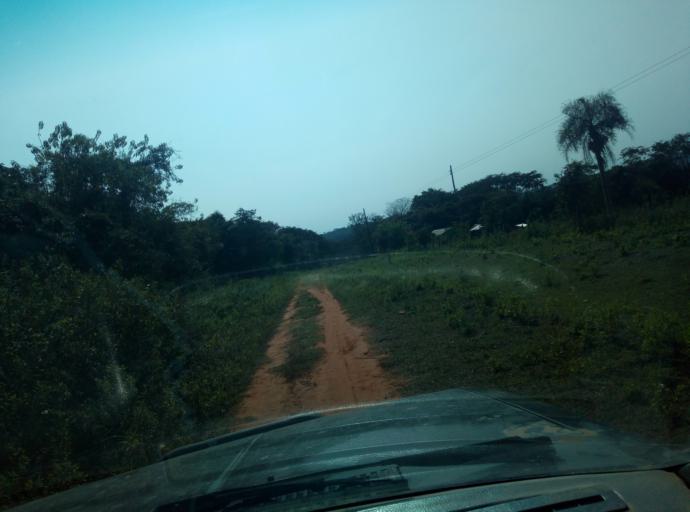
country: PY
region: Caaguazu
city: Carayao
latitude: -25.3037
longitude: -56.3240
